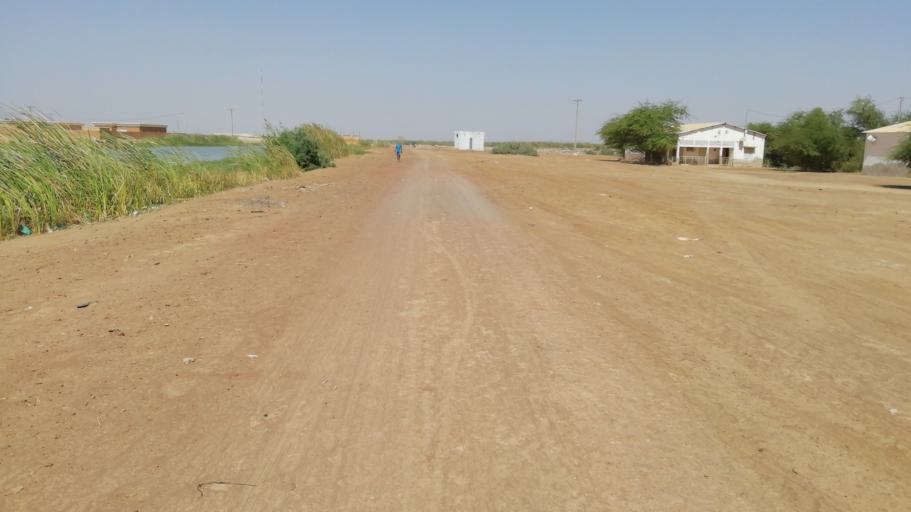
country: SN
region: Saint-Louis
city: Rosso
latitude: 16.3991
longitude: -16.0737
